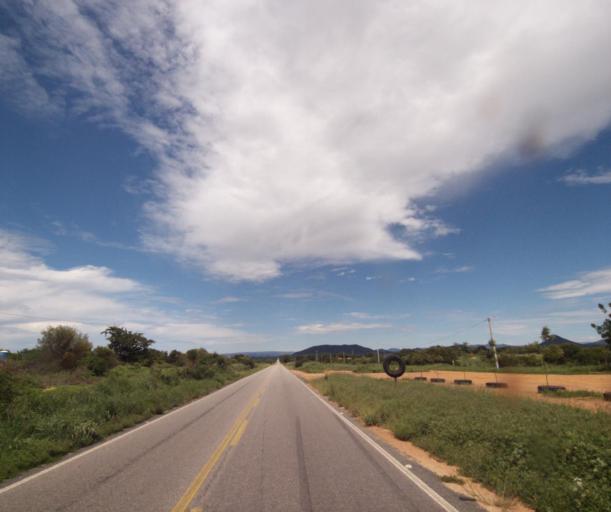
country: BR
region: Bahia
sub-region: Guanambi
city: Guanambi
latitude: -14.2307
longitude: -42.9371
